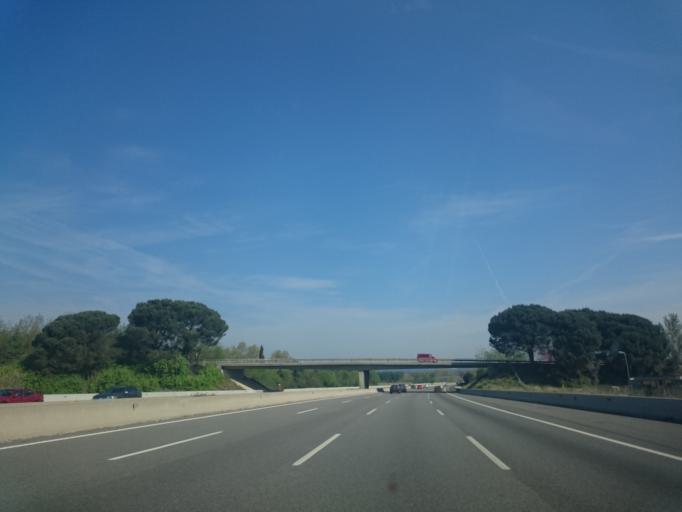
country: ES
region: Catalonia
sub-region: Provincia de Girona
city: Vilablareix
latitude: 41.9711
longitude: 2.7785
